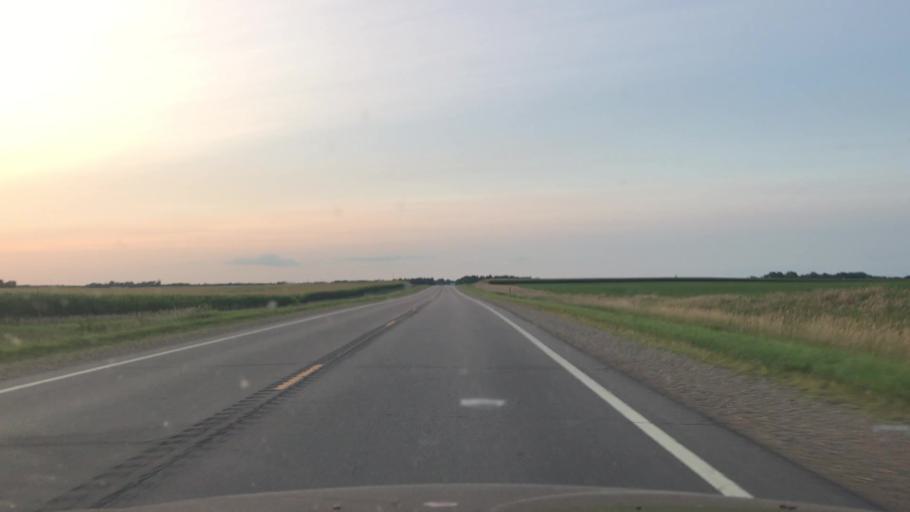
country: US
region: Minnesota
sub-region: Redwood County
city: Redwood Falls
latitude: 44.5030
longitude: -95.1178
